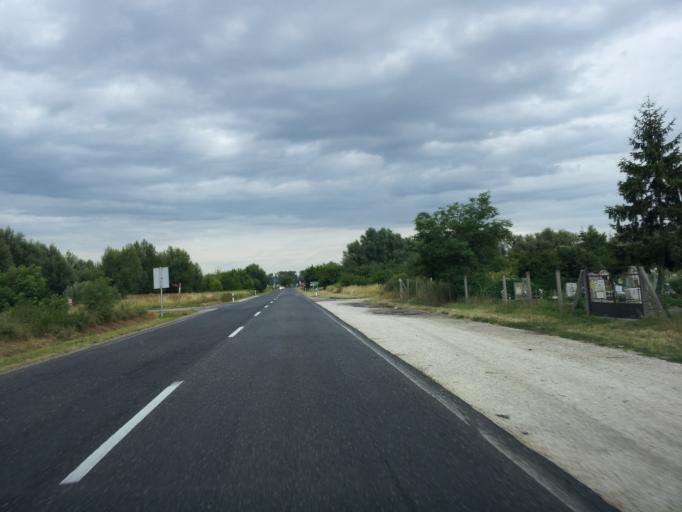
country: HU
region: Veszprem
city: Devecser
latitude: 47.1253
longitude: 17.3710
